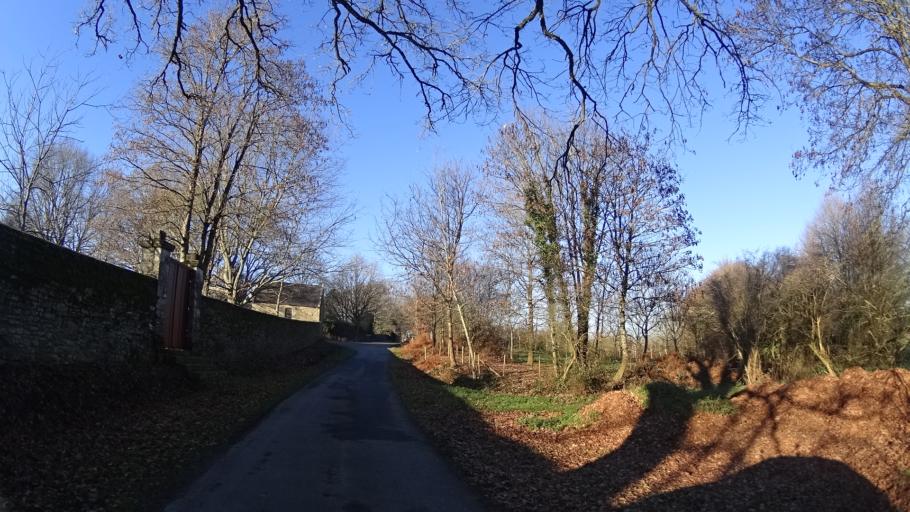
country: FR
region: Brittany
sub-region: Departement du Morbihan
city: Allaire
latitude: 47.6680
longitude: -2.1807
